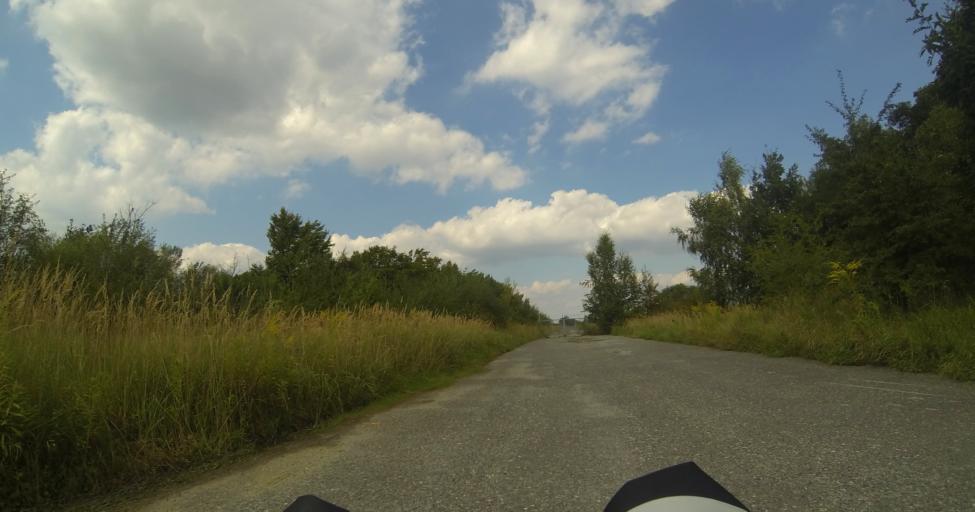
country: DE
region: Saxony
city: Grossenhain
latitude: 51.3110
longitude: 13.5385
